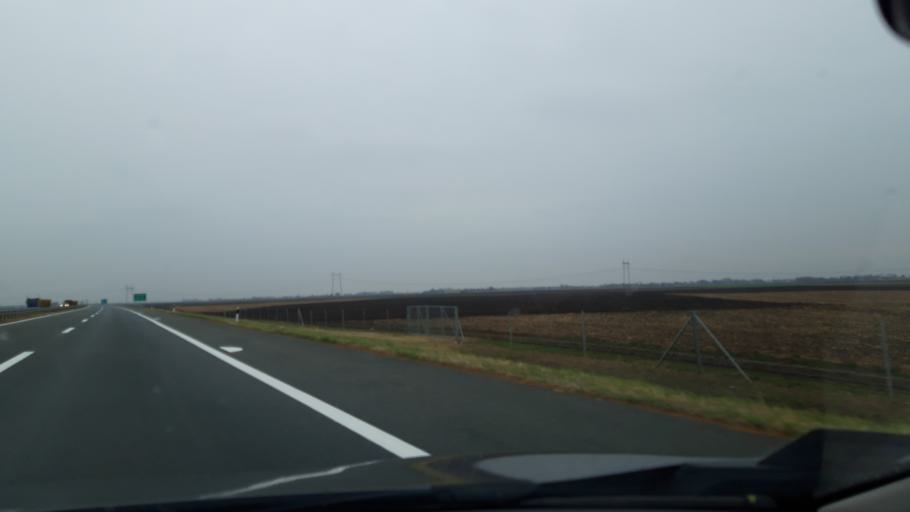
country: RS
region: Autonomna Pokrajina Vojvodina
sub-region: Severnobacki Okrug
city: Subotica
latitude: 46.0063
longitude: 19.7269
